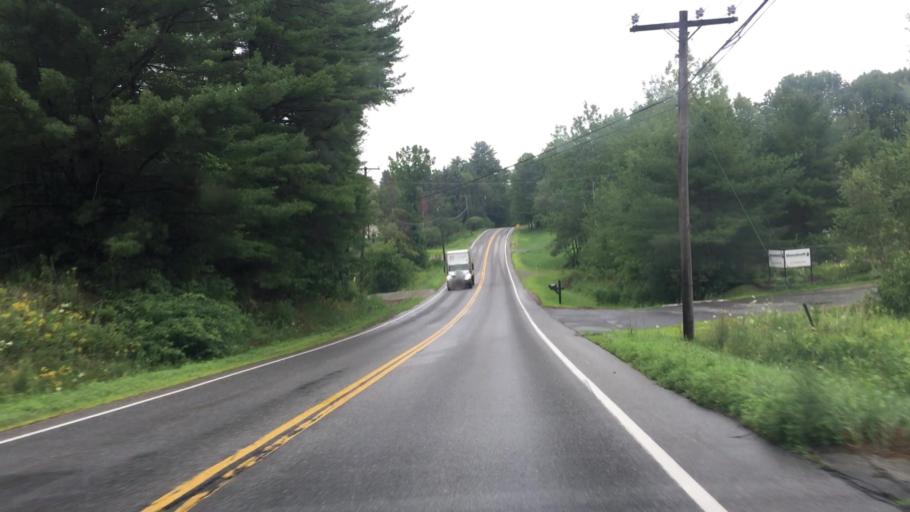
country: US
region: Maine
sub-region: Kennebec County
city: Augusta
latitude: 44.3355
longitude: -69.8147
